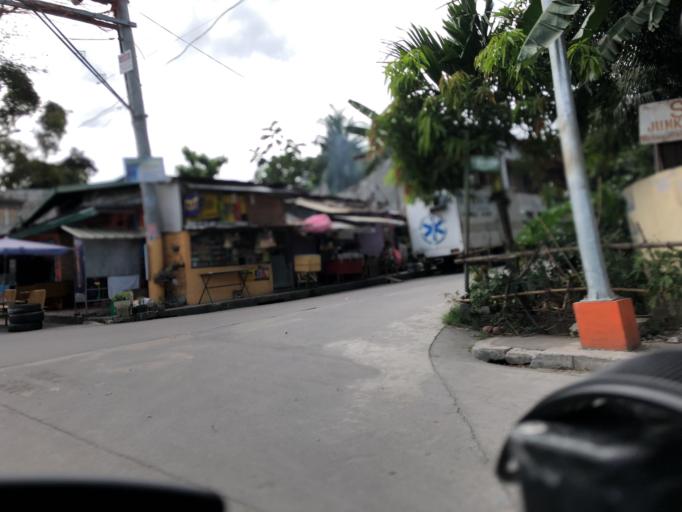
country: PH
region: Central Luzon
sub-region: Province of Bulacan
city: San Jose del Monte
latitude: 14.7496
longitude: 121.0572
